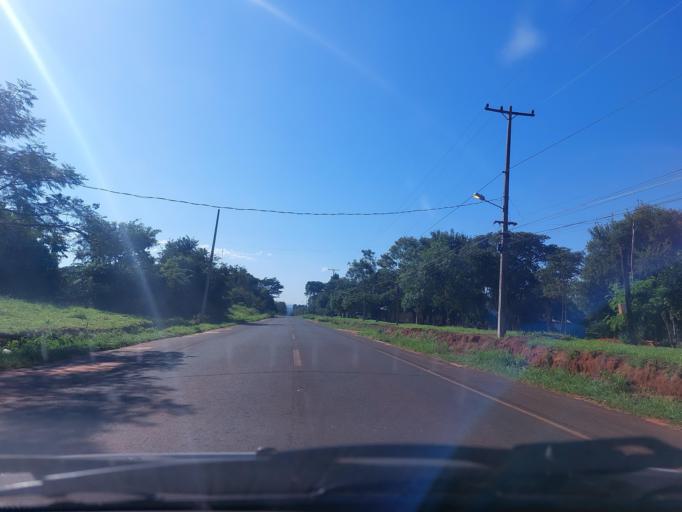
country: PY
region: San Pedro
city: Guayaybi
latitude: -24.5315
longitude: -56.4407
